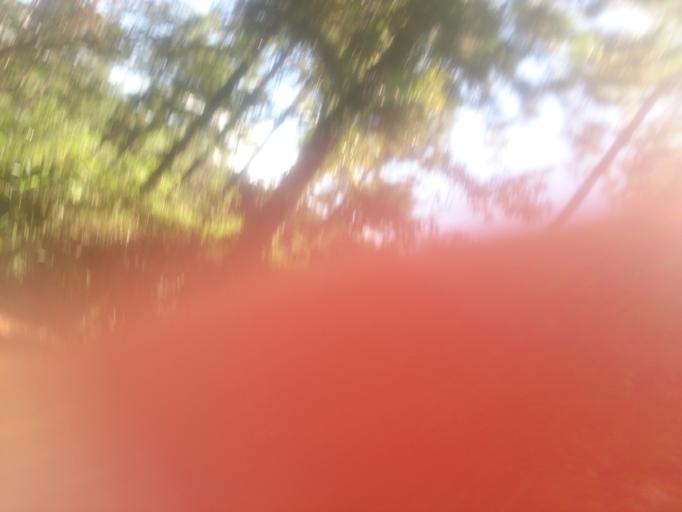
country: AR
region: Misiones
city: General Alvear
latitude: -27.4341
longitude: -55.1143
